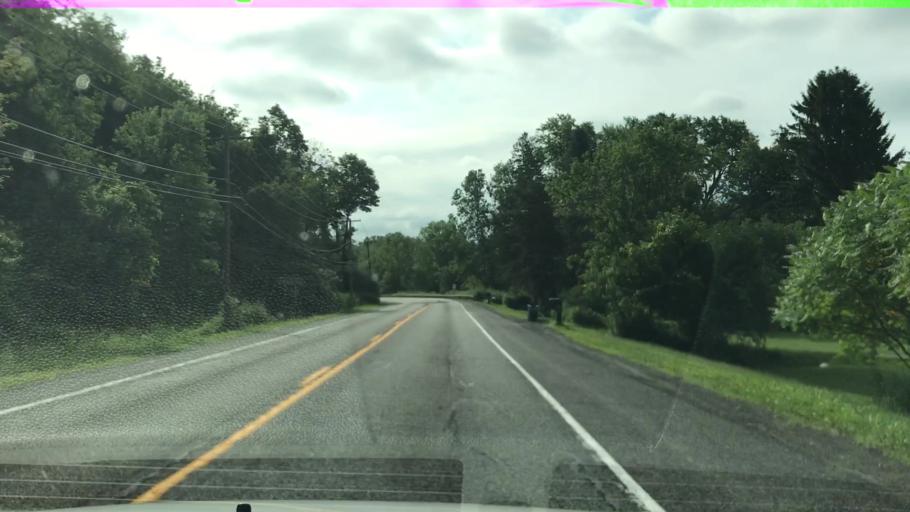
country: US
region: New York
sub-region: Erie County
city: Alden
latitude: 42.8417
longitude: -78.4660
